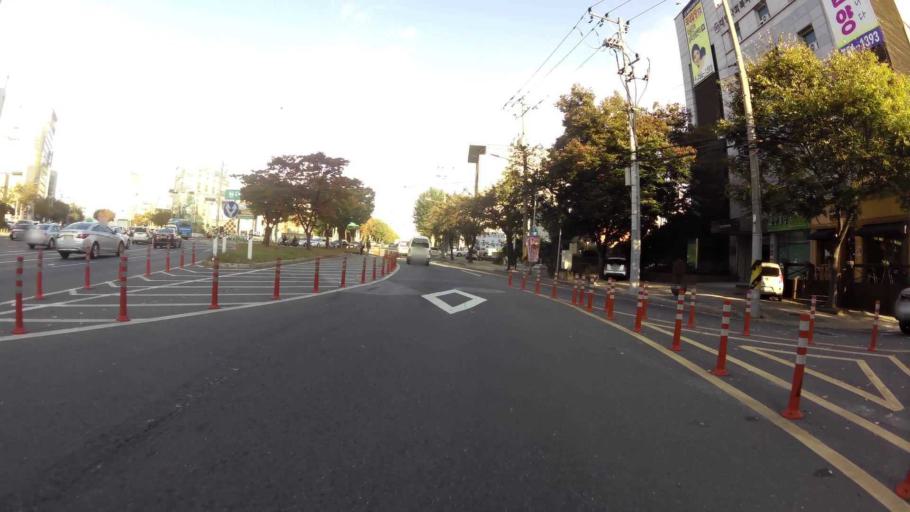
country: KR
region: Daegu
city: Daegu
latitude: 35.8666
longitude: 128.6295
